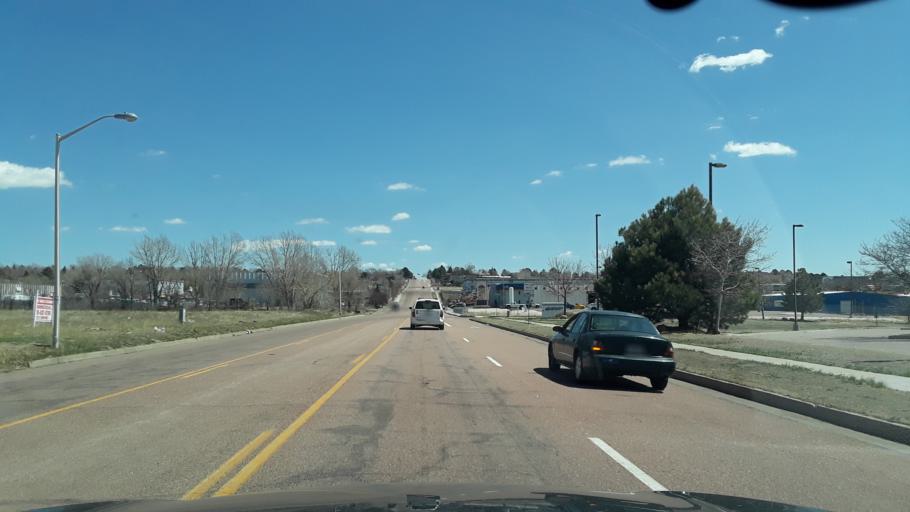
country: US
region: Colorado
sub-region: El Paso County
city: Cimarron Hills
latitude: 38.8462
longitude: -104.7171
